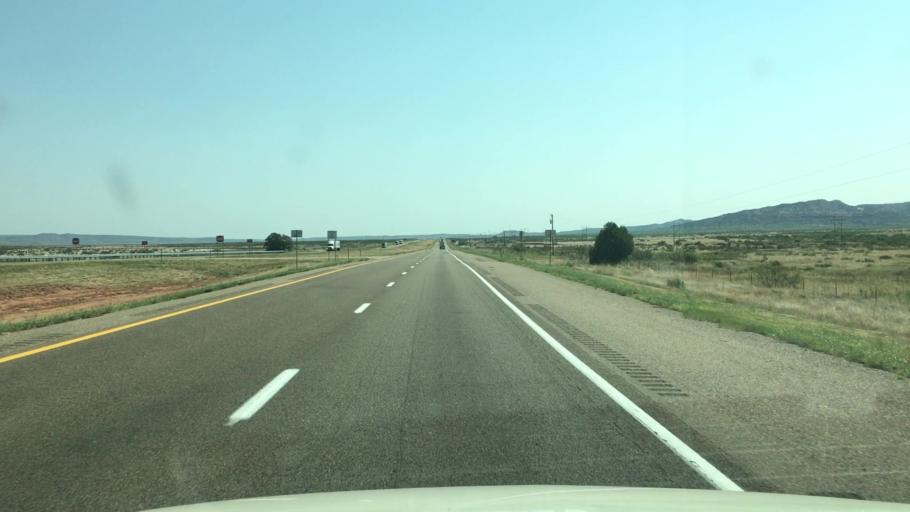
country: US
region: New Mexico
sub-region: Quay County
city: Tucumcari
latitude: 35.1000
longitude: -104.0483
